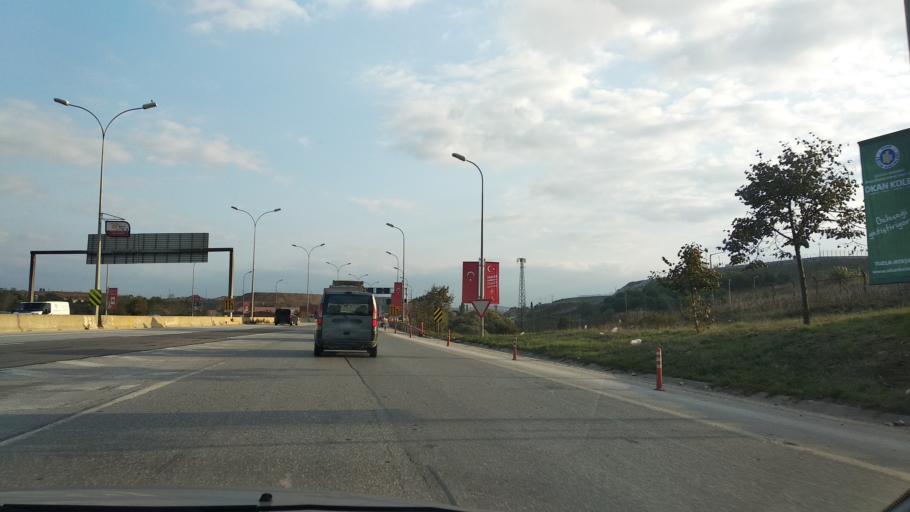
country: TR
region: Istanbul
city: Pendik
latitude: 40.9114
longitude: 29.3261
